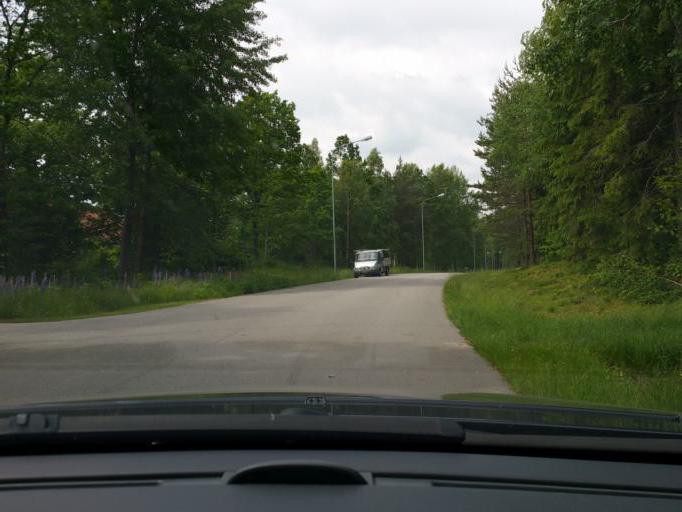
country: SE
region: Kronoberg
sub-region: Vaxjo Kommun
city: Lammhult
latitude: 57.1722
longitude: 14.6082
